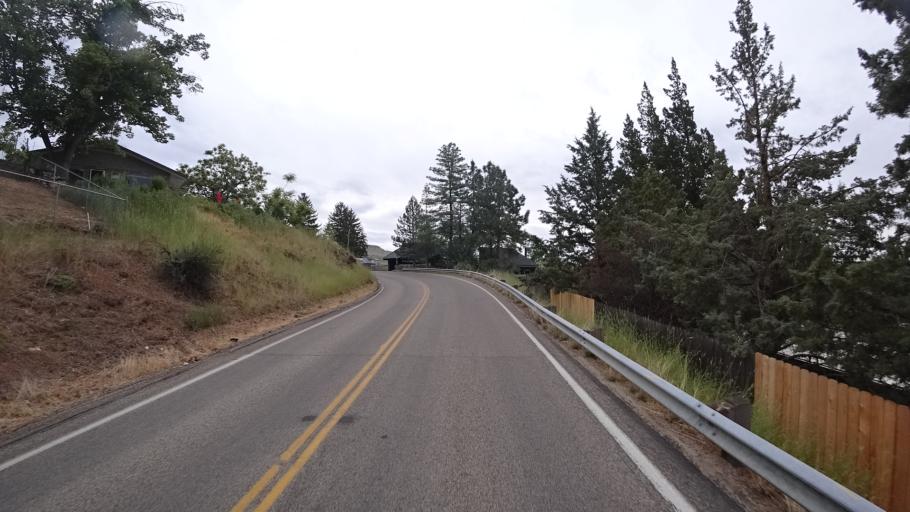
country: US
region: Idaho
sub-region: Ada County
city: Boise
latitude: 43.6133
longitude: -116.1801
